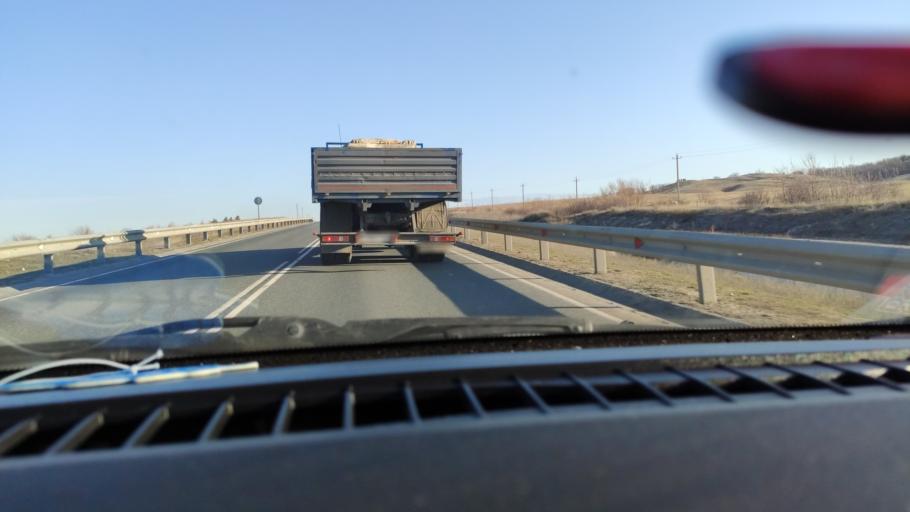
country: RU
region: Saratov
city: Alekseyevka
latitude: 52.3187
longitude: 47.9224
